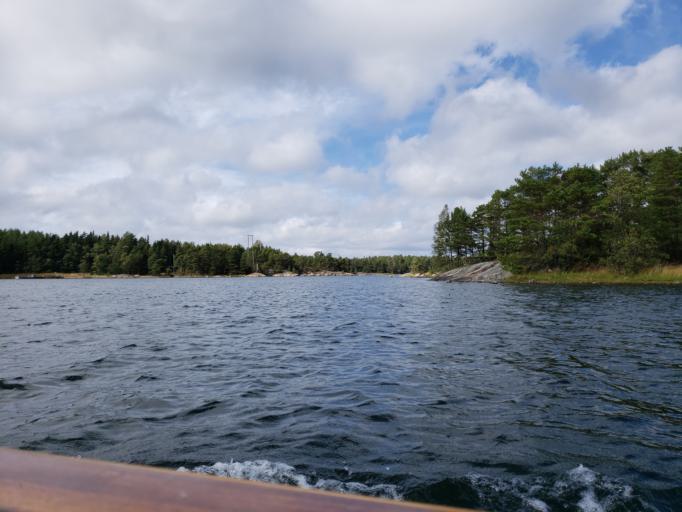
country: FI
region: Varsinais-Suomi
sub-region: Aboland-Turunmaa
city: Dragsfjaerd
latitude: 59.9167
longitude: 22.3878
